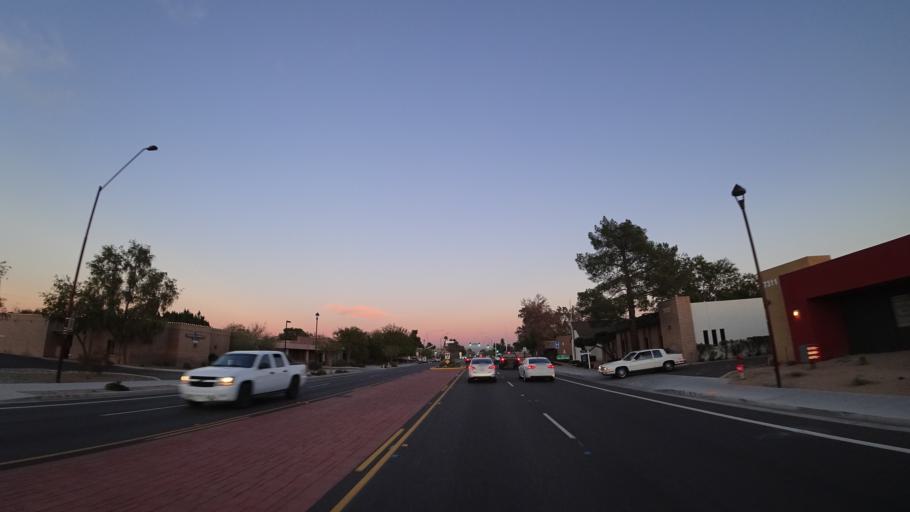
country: US
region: Arizona
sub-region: Maricopa County
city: Scottsdale
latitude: 33.4803
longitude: -111.9234
